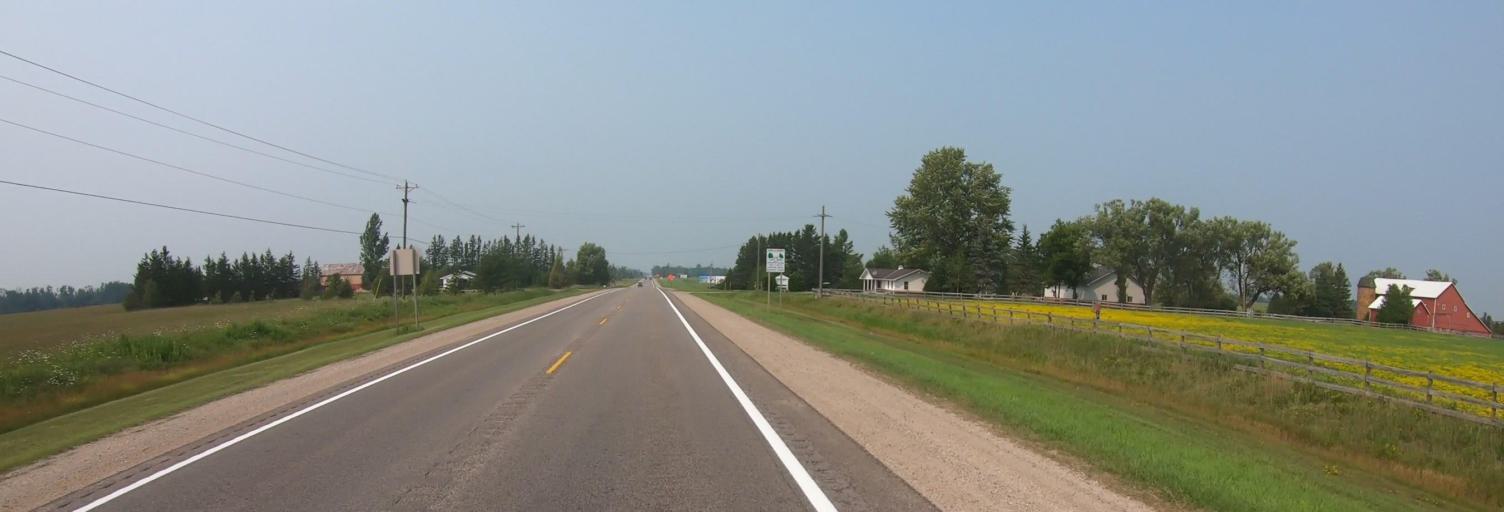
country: US
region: Michigan
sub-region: Chippewa County
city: Sault Ste. Marie
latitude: 46.1313
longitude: -84.3633
